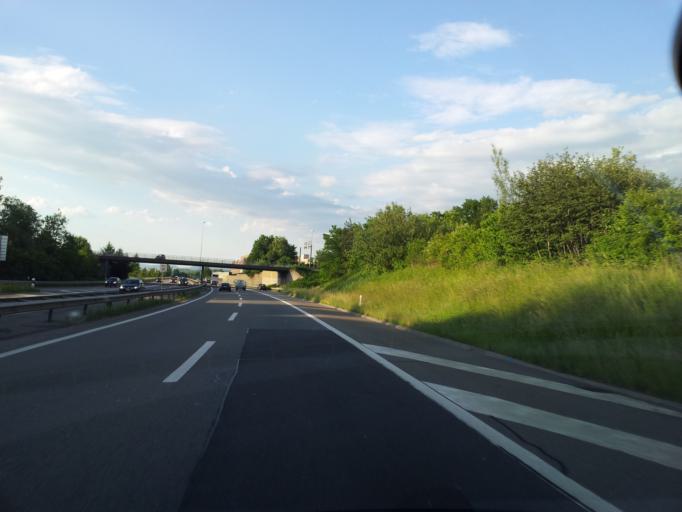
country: CH
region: Lucerne
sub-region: Lucerne-Land District
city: Root
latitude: 47.1235
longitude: 8.3933
